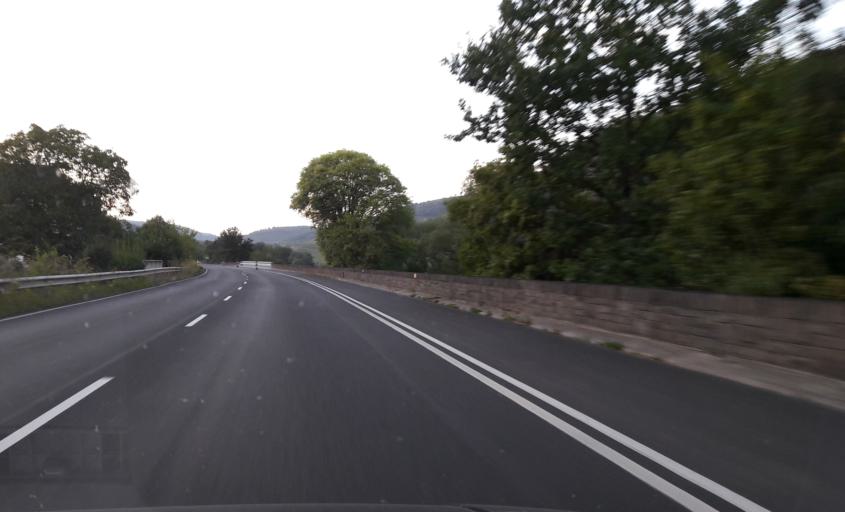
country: DE
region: Rheinland-Pfalz
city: Briedel
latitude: 50.0215
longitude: 7.1514
